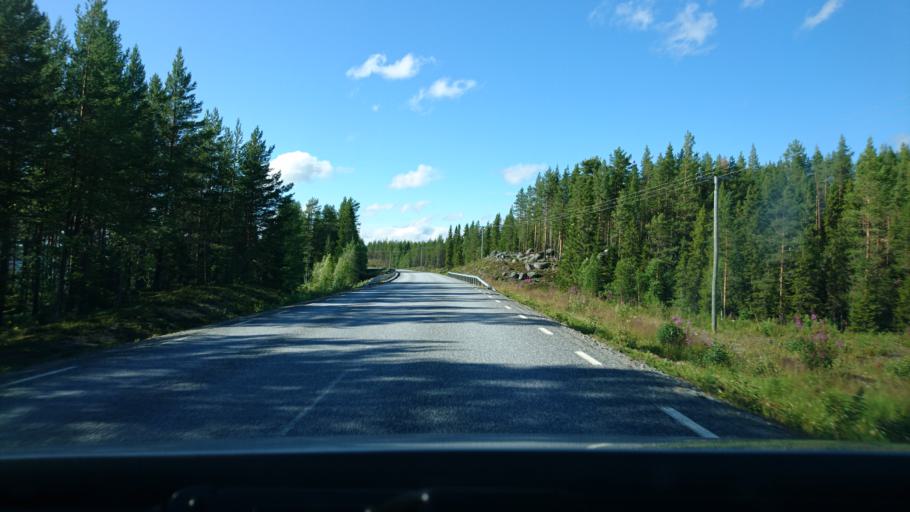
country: SE
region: Vaesterbotten
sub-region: Asele Kommun
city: Asele
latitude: 64.3358
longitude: 17.0505
